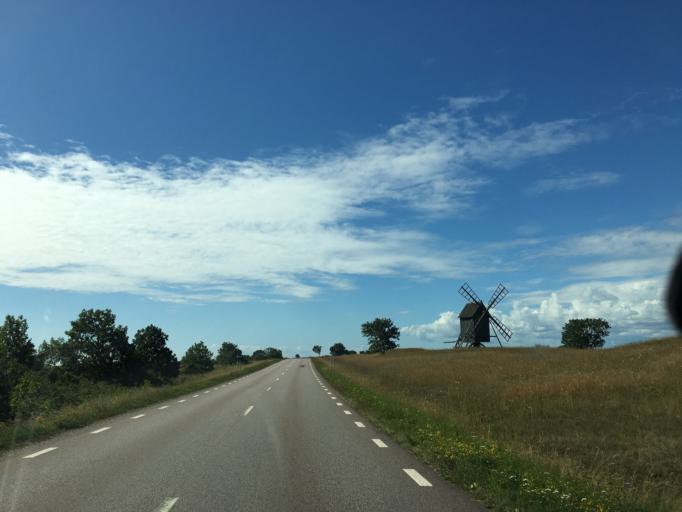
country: SE
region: Kalmar
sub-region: Morbylanga Kommun
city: Moerbylanga
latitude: 56.5355
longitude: 16.4452
